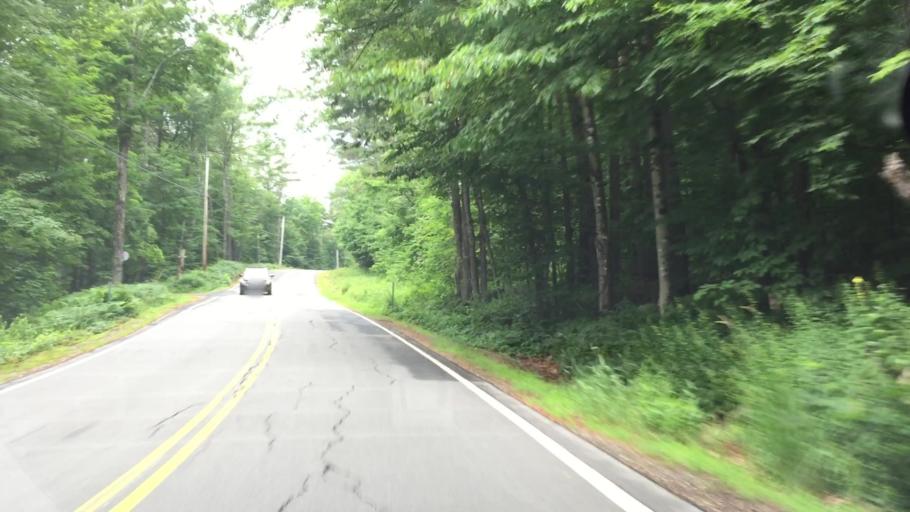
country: US
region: New Hampshire
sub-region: Carroll County
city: Sandwich
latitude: 43.8027
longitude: -71.4914
